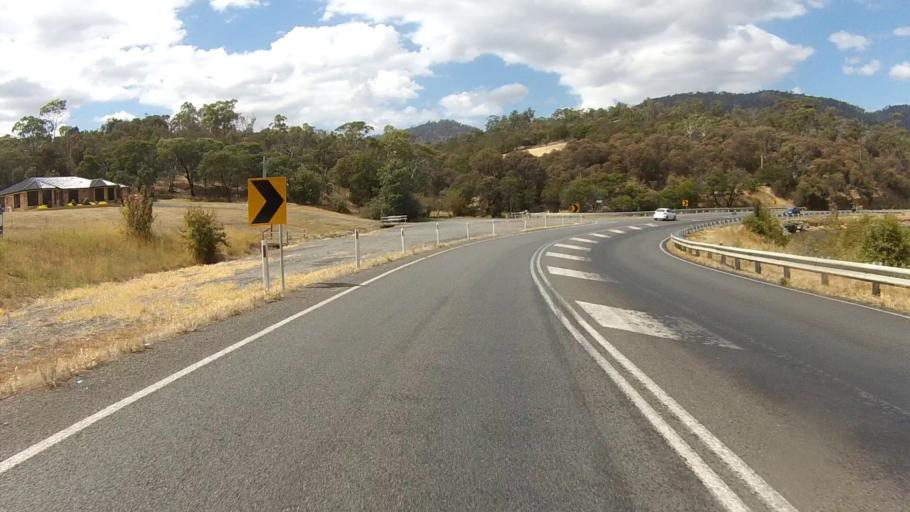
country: AU
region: Tasmania
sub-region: Brighton
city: Old Beach
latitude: -42.7776
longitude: 147.2835
